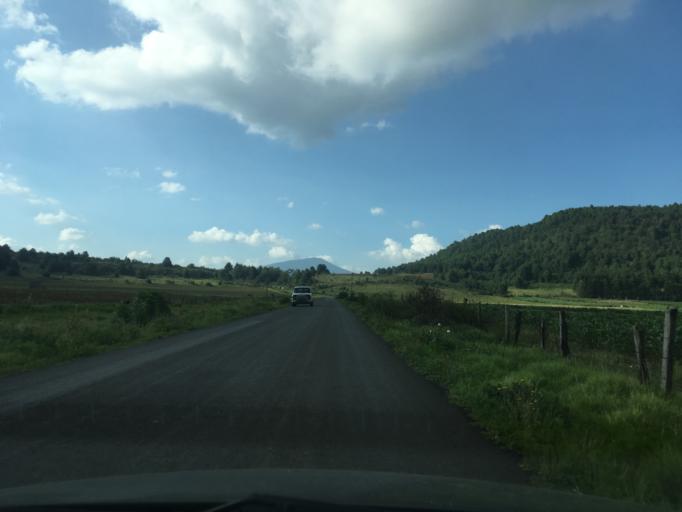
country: MX
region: Michoacan
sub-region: Nahuatzen
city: Sevina
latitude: 19.6239
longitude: -101.9281
